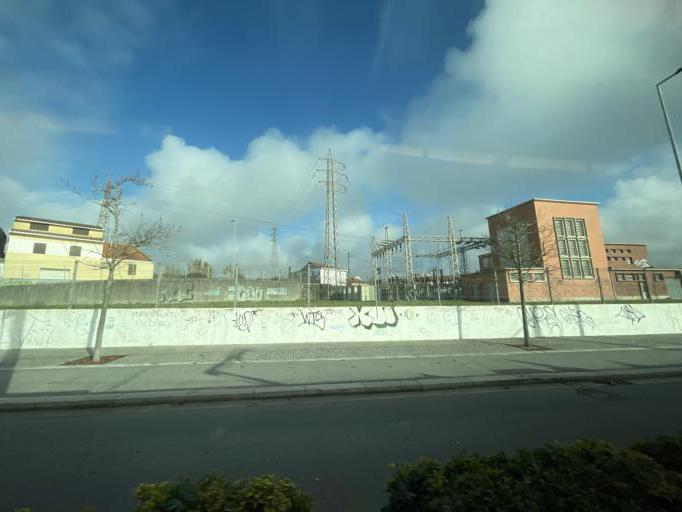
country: PT
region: Porto
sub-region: Vila do Conde
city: Vila do Conde
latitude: 41.3554
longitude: -8.7367
